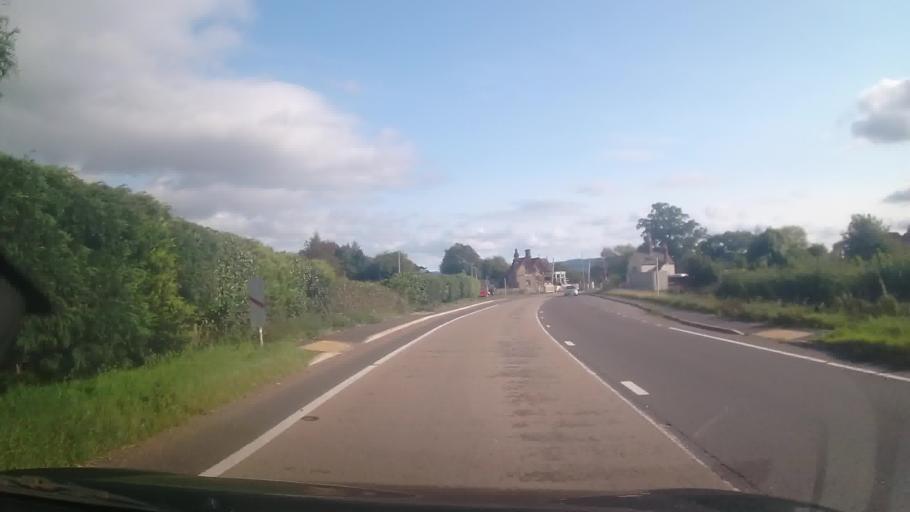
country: GB
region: England
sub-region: Shropshire
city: Bromfield
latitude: 52.4085
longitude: -2.8046
